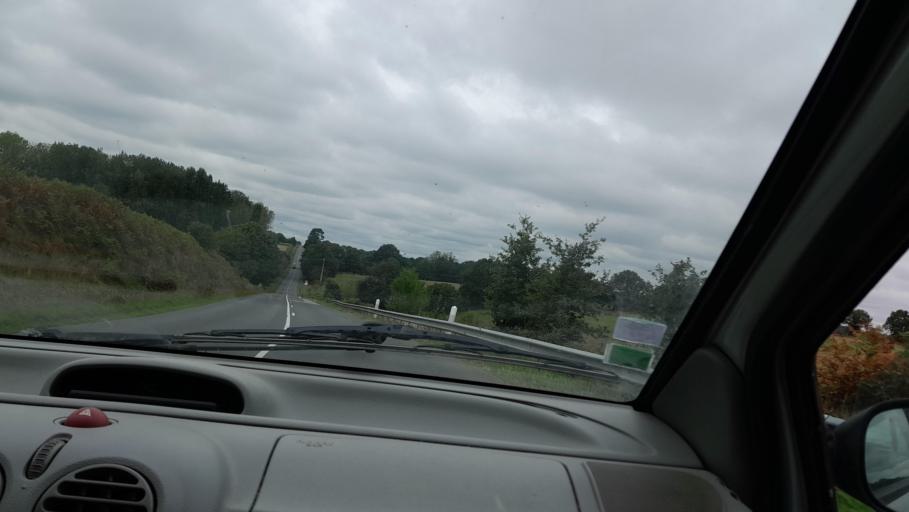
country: FR
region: Pays de la Loire
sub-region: Departement de la Mayenne
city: Cosse-le-Vivien
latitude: 47.9544
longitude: -0.9357
